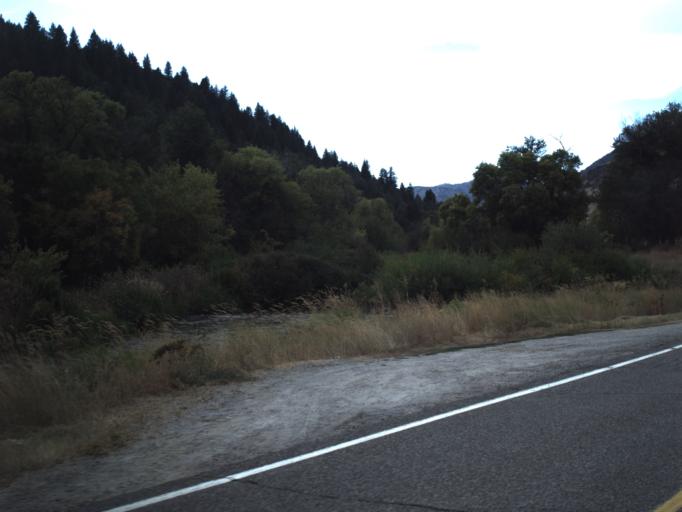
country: US
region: Utah
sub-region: Cache County
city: Millville
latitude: 41.6128
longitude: -111.6334
